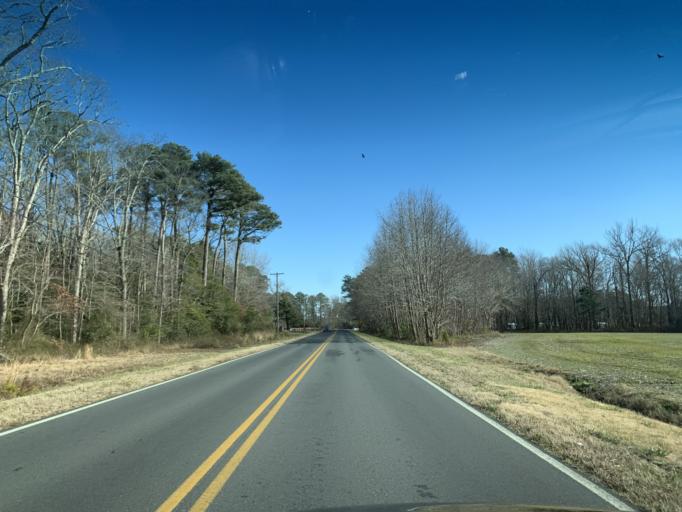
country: US
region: Maryland
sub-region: Worcester County
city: Ocean Pines
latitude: 38.4165
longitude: -75.1250
